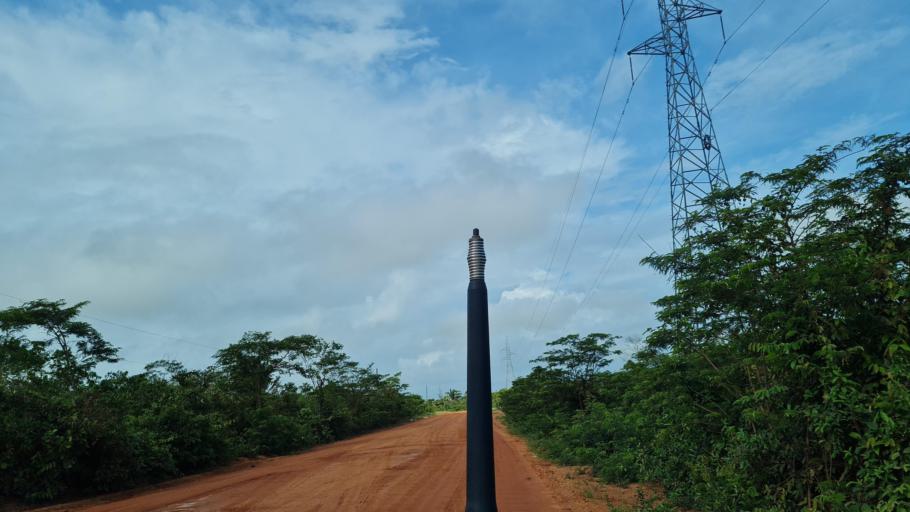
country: NI
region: Atlantico Norte (RAAN)
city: Puerto Cabezas
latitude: 14.1240
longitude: -83.5417
